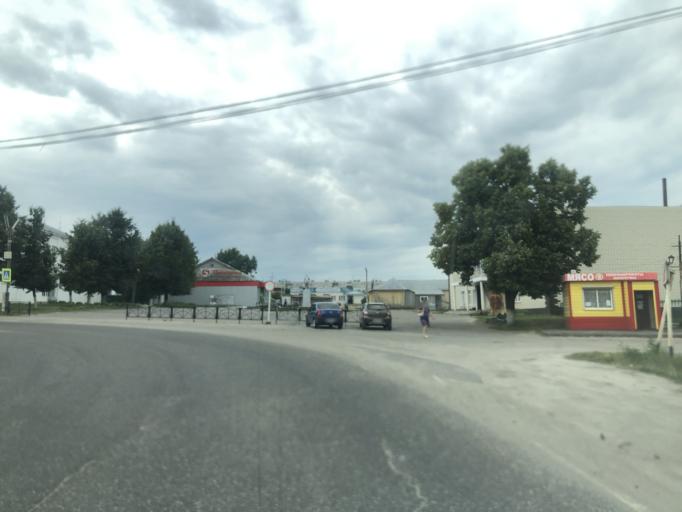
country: RU
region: Ivanovo
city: Pestyaki
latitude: 56.7077
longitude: 42.6700
